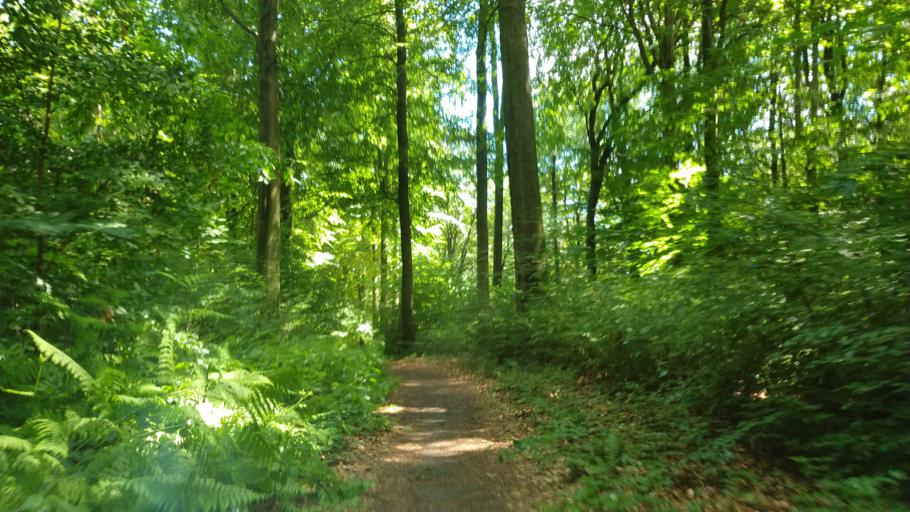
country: BE
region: Flanders
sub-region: Provincie Vlaams-Brabant
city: Bierbeek
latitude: 50.8131
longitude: 4.7323
